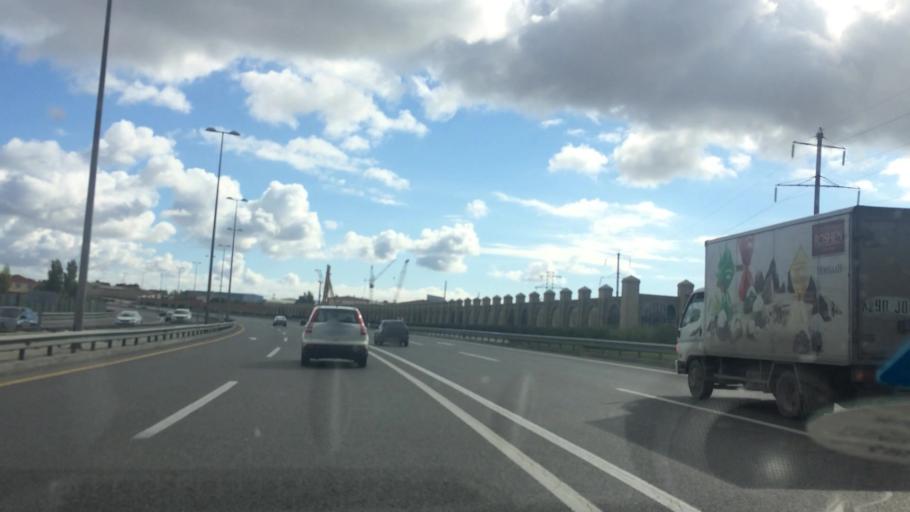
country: AZ
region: Baki
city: Ramana
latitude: 40.4385
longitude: 49.9764
